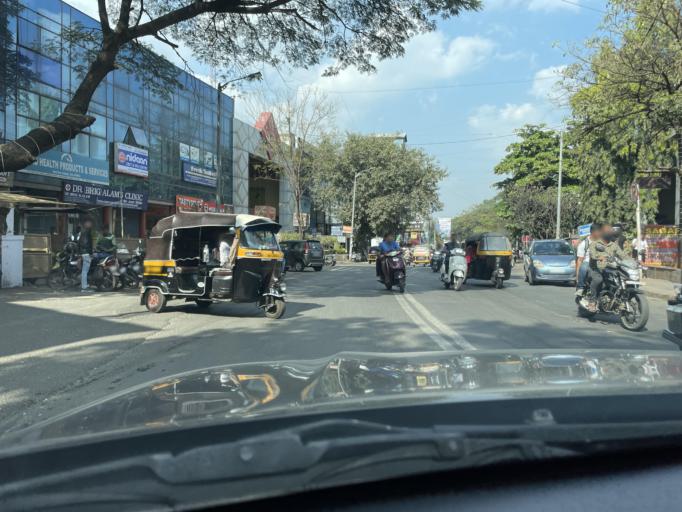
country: IN
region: Maharashtra
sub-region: Pune Division
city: Pune
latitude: 18.4934
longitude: 73.8998
